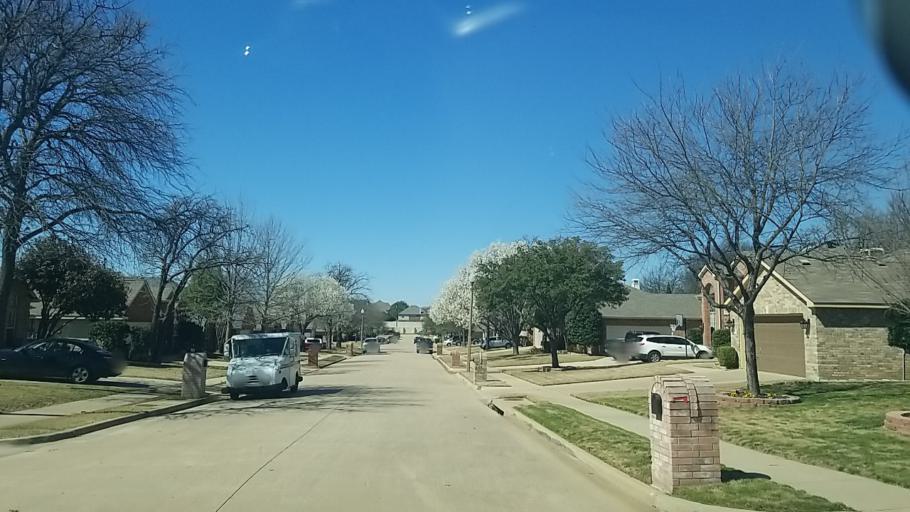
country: US
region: Texas
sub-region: Denton County
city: Corinth
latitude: 33.1595
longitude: -97.0899
